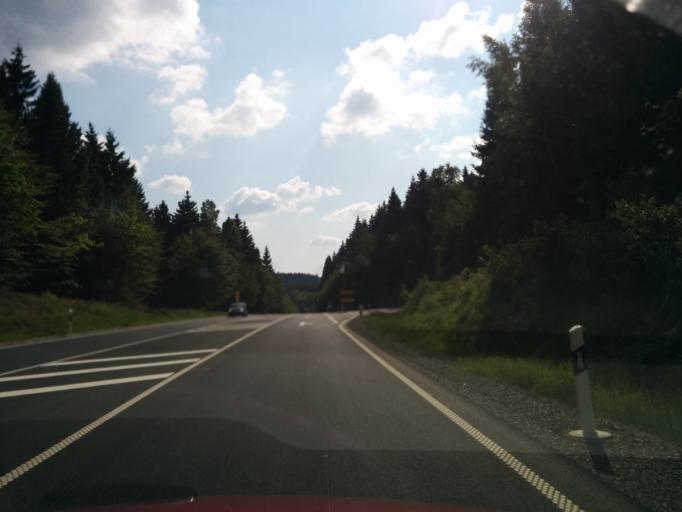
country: DE
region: Lower Saxony
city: Braunlage
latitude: 51.7155
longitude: 10.5992
